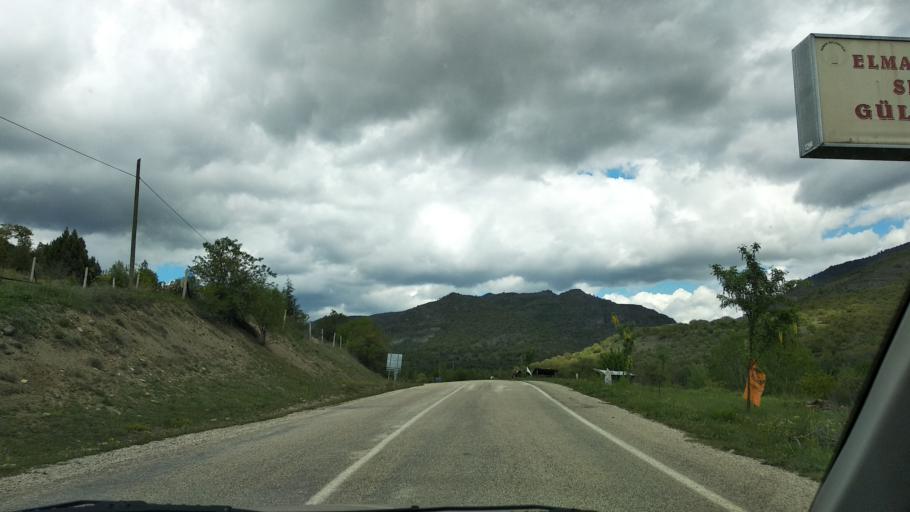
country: TR
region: Bolu
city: Seben
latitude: 40.4209
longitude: 31.5846
